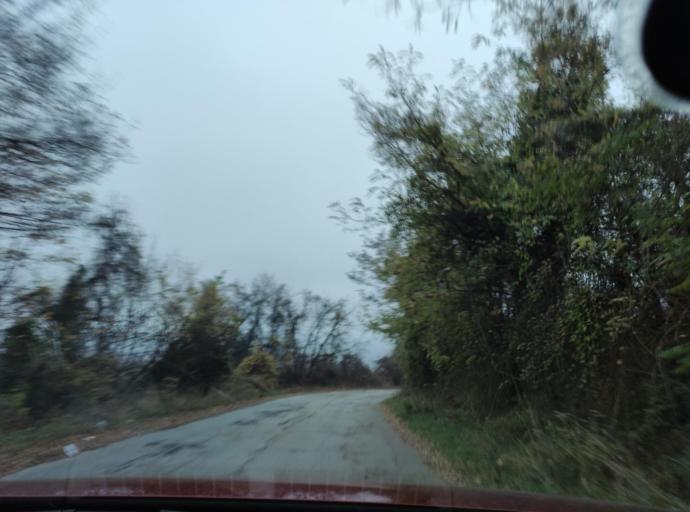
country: BG
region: Lovech
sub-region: Obshtina Yablanitsa
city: Yablanitsa
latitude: 43.1003
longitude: 24.0725
